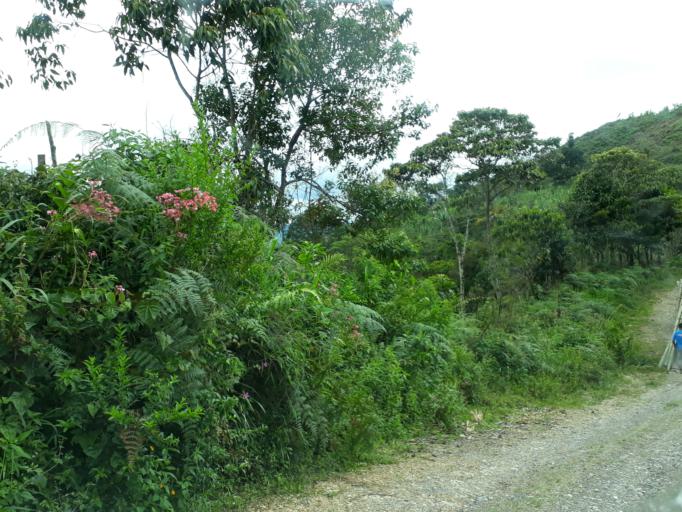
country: CO
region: Boyaca
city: Quipama
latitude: 5.3936
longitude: -74.1156
